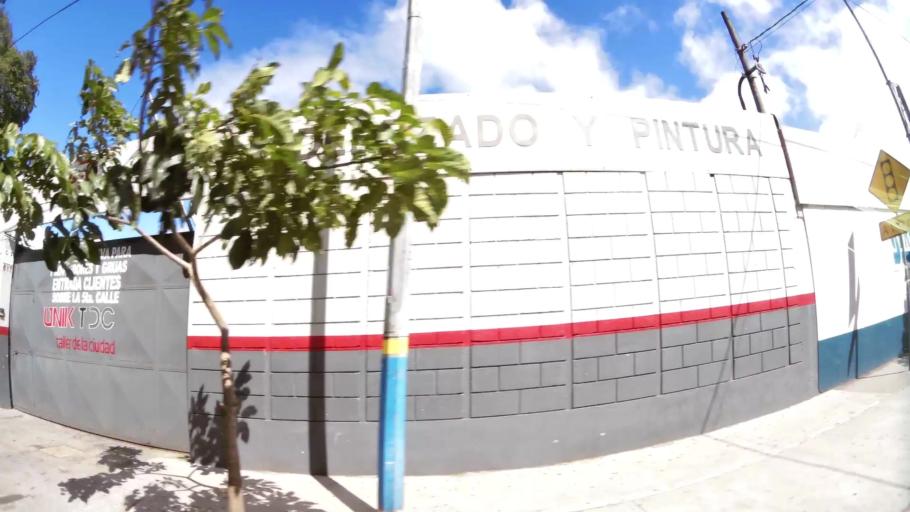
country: GT
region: Guatemala
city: Guatemala City
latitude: 14.6092
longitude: -90.5184
